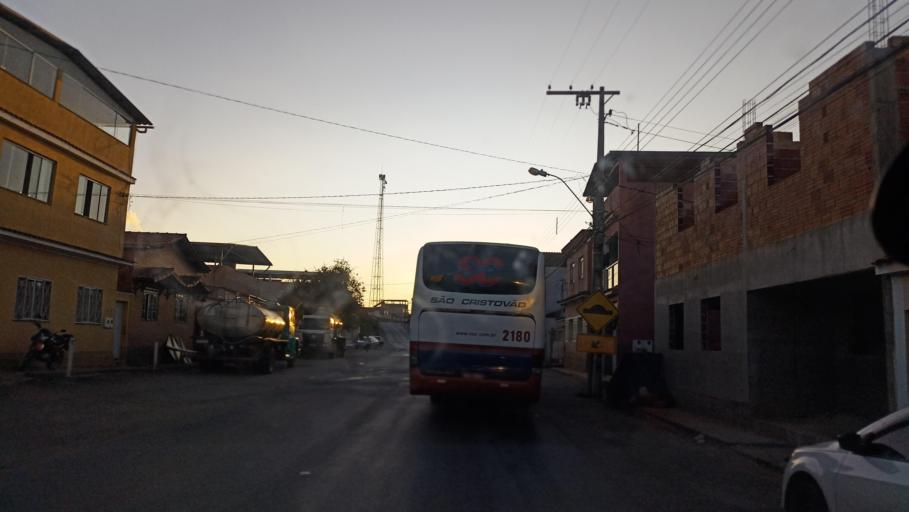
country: BR
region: Minas Gerais
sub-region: Sao Joao Del Rei
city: Sao Joao del Rei
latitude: -21.2439
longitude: -44.4121
